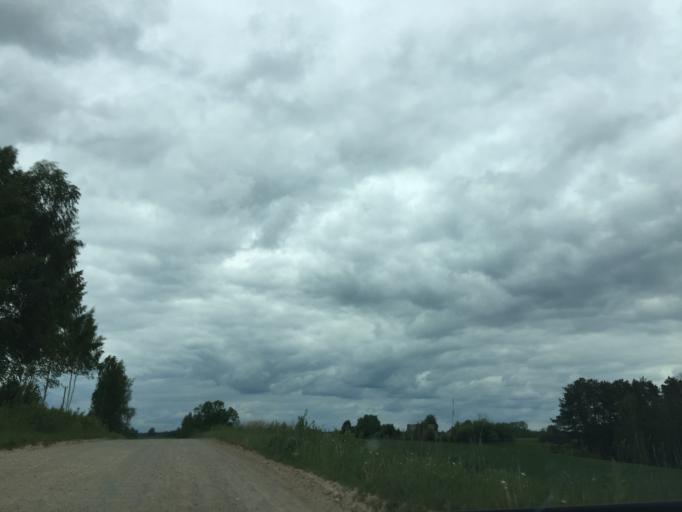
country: LV
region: Dagda
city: Dagda
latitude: 56.0238
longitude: 27.5959
